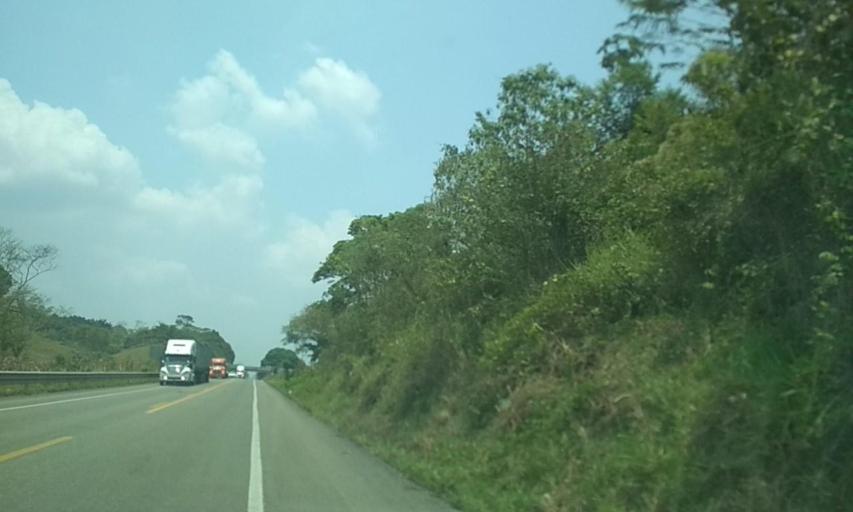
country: MX
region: Tabasco
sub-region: Huimanguillo
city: Francisco Rueda
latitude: 17.6717
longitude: -93.8717
